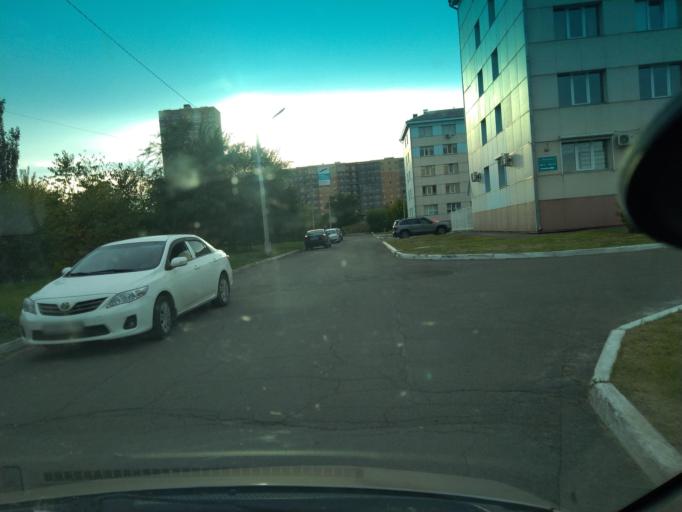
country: RU
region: Krasnoyarskiy
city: Krasnoyarsk
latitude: 56.0321
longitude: 92.8871
